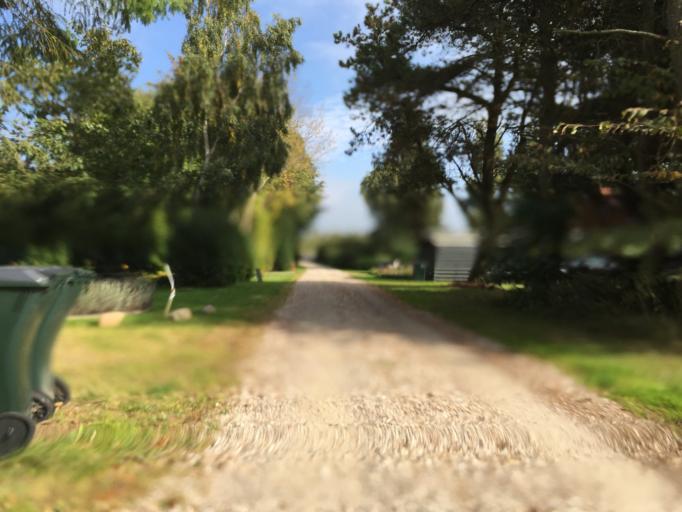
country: DK
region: Zealand
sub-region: Odsherred Kommune
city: Hojby
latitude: 55.8996
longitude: 11.5627
